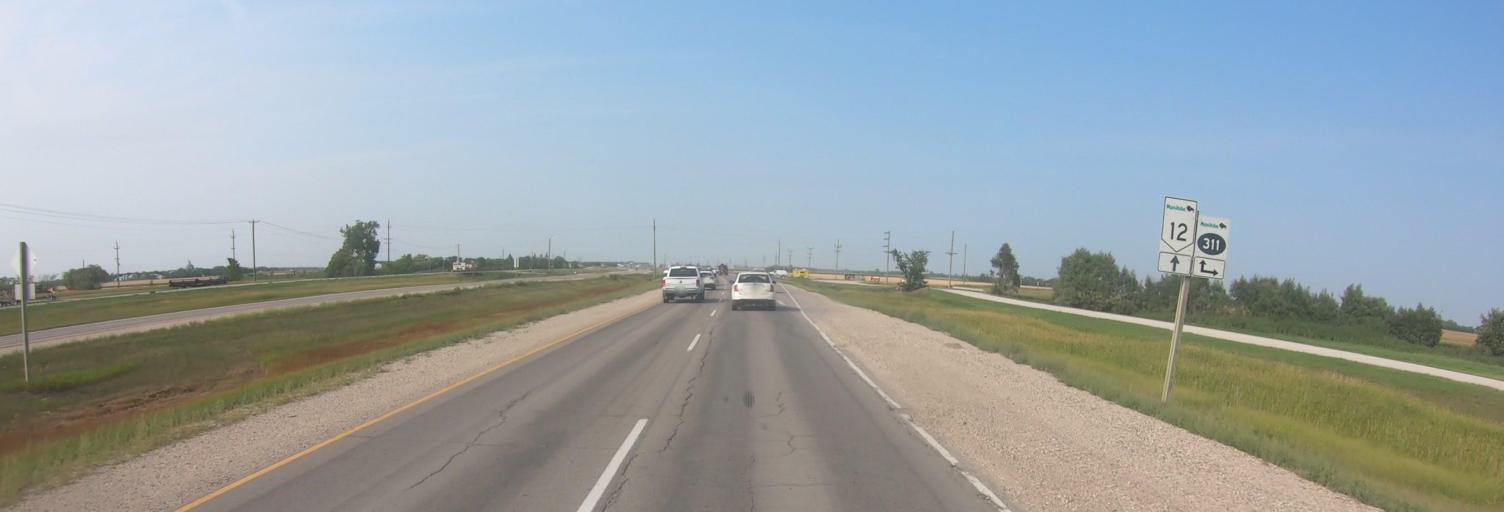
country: CA
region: Manitoba
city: Steinbach
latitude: 49.5729
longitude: -96.6868
